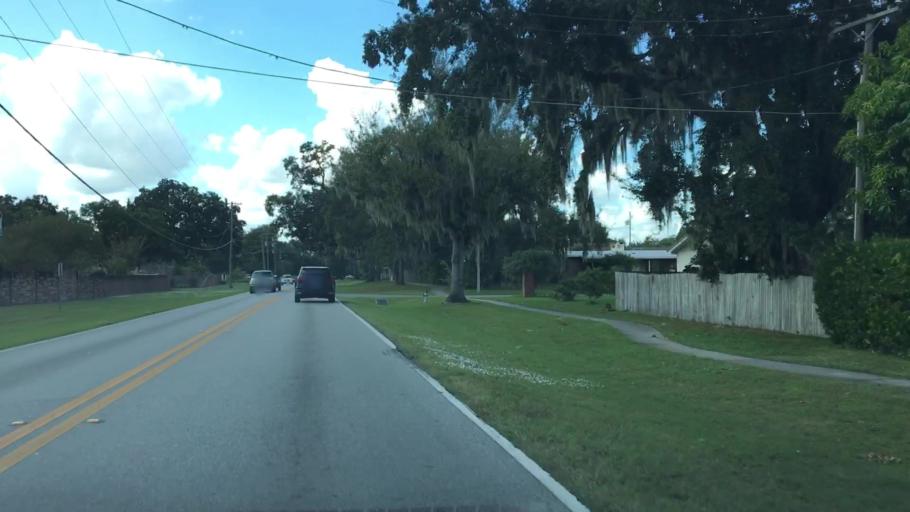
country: US
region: Florida
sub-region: Orange County
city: Conway
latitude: 28.4805
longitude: -81.3414
